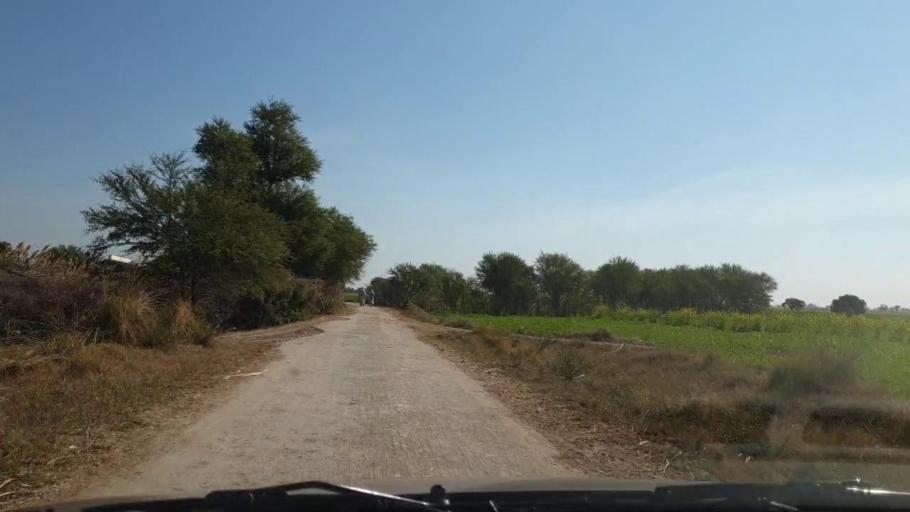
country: PK
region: Sindh
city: Sinjhoro
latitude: 26.1334
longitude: 68.8386
